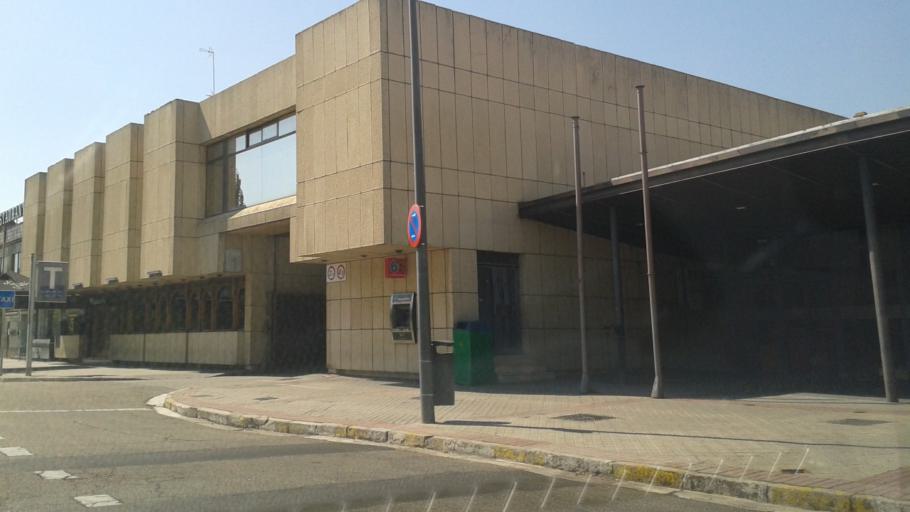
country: ES
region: Castille and Leon
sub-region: Provincia de Valladolid
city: Valladolid
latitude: 41.6555
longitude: -4.7379
